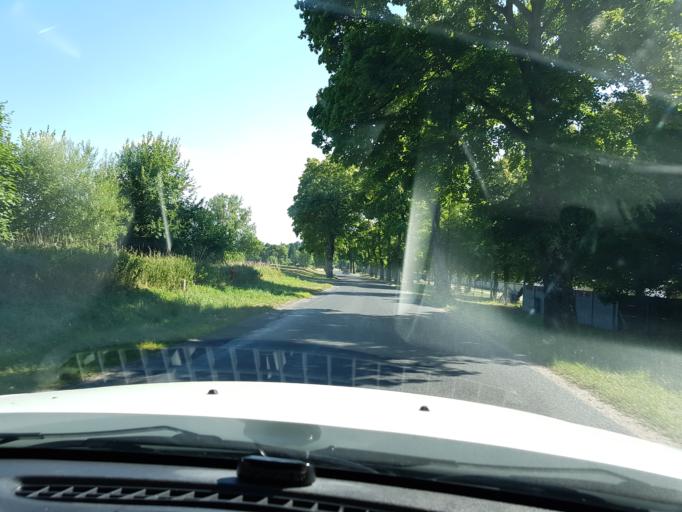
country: PL
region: West Pomeranian Voivodeship
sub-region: Powiat bialogardzki
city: Karlino
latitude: 53.9625
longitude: 15.9006
